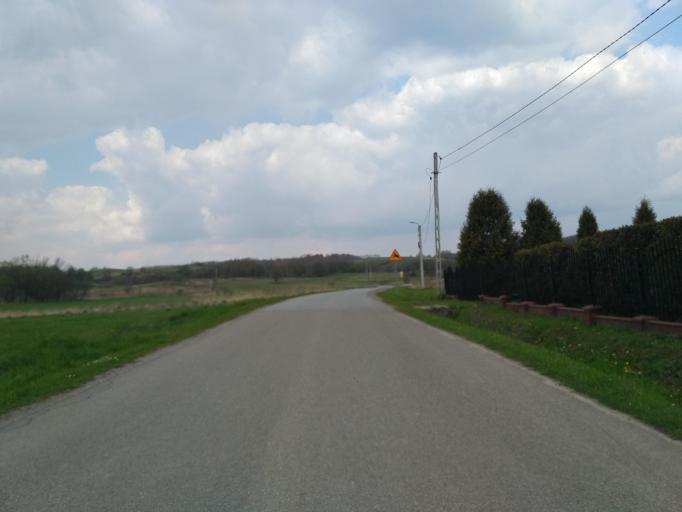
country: PL
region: Subcarpathian Voivodeship
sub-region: Powiat sanocki
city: Strachocina
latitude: 49.6133
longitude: 22.0745
